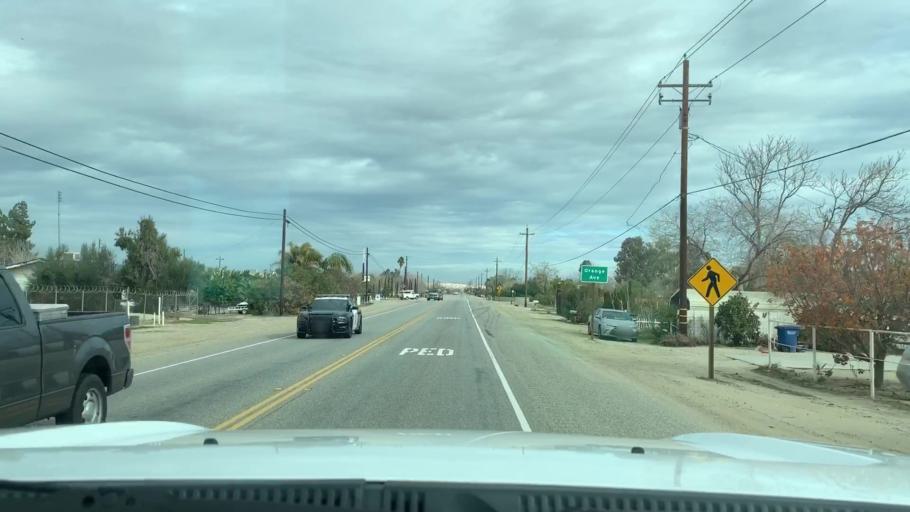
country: US
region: California
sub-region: Kern County
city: Ford City
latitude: 35.2064
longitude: -119.4099
